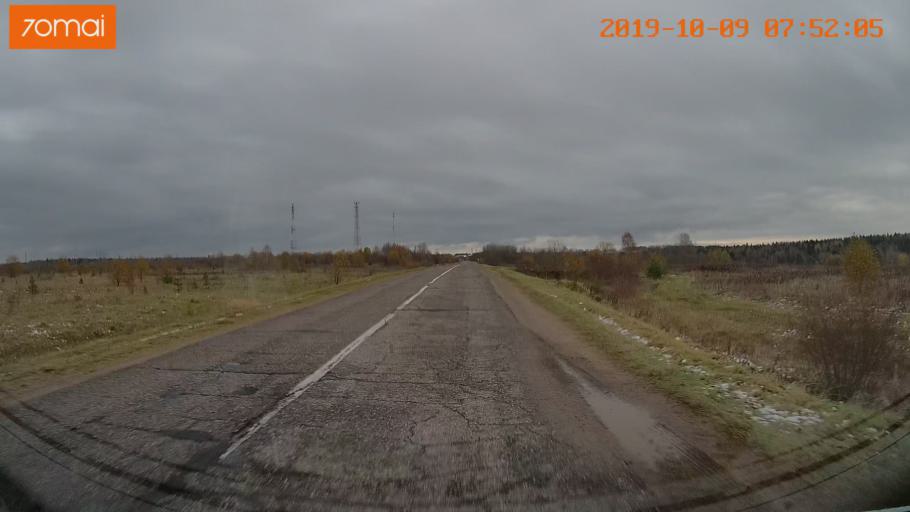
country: RU
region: Jaroslavl
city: Kukoboy
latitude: 58.6882
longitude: 39.8829
